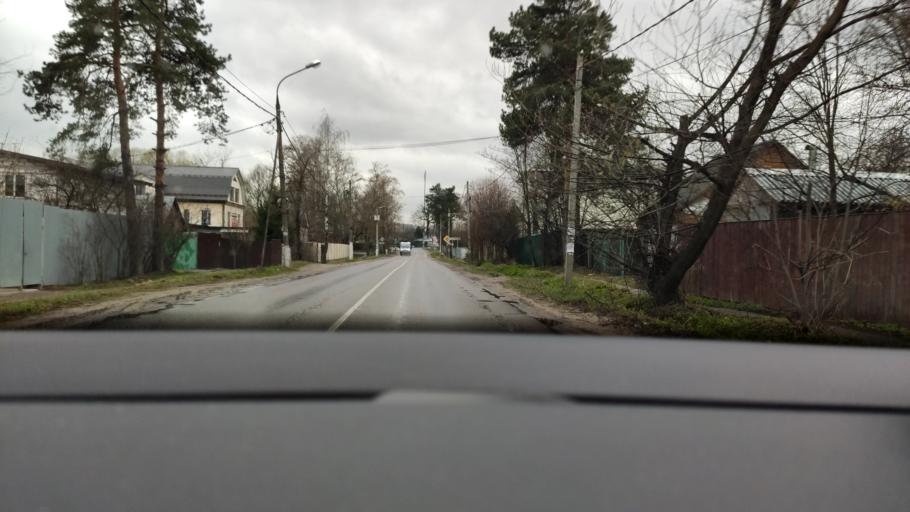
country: RU
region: Moskovskaya
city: Saltykovka
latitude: 55.7714
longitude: 37.8960
